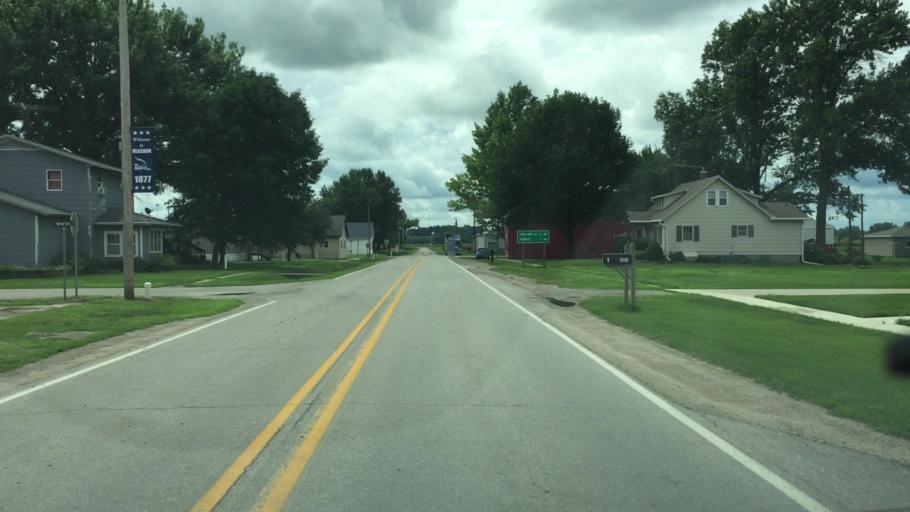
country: US
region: Iowa
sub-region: Jasper County
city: Monroe
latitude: 41.5783
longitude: -93.0235
